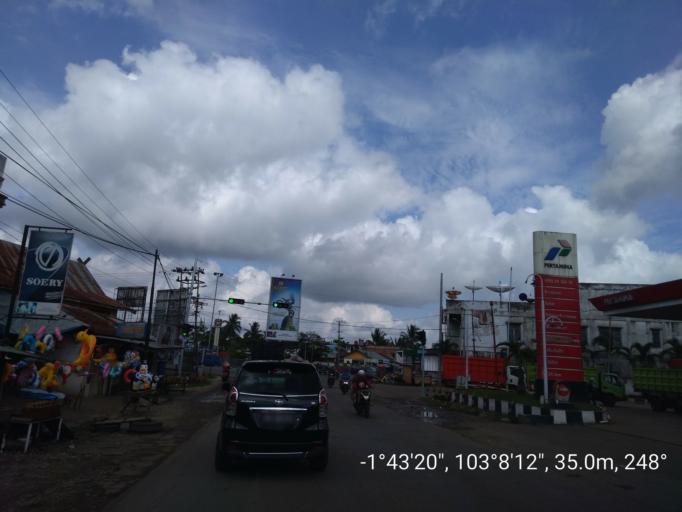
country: ID
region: Jambi
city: Muara Tembesi
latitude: -1.7224
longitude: 103.1369
